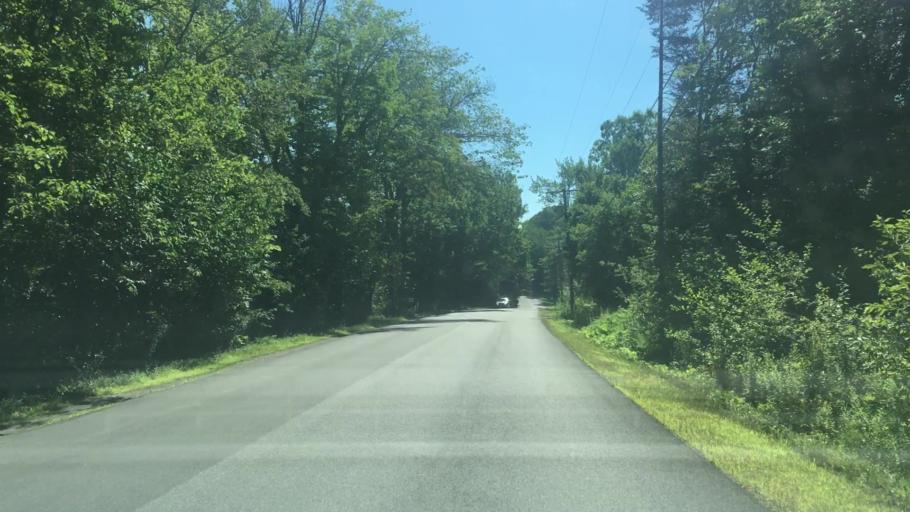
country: US
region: Maine
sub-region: Waldo County
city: Northport
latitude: 44.3818
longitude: -68.9766
